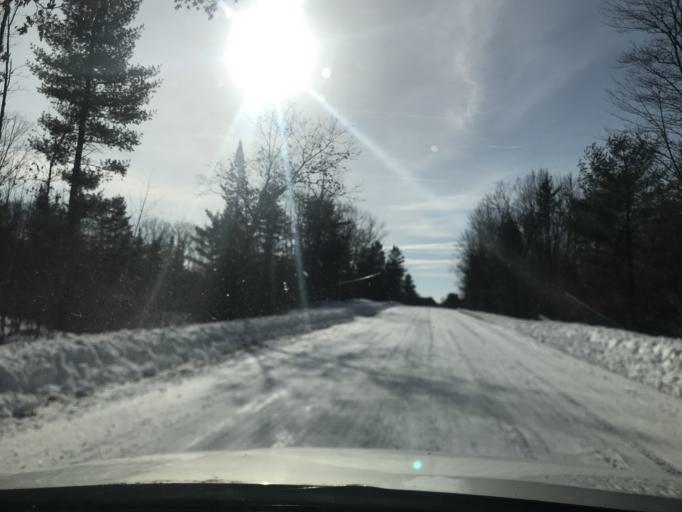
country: US
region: Wisconsin
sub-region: Oconto County
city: Gillett
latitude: 45.1487
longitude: -88.2406
